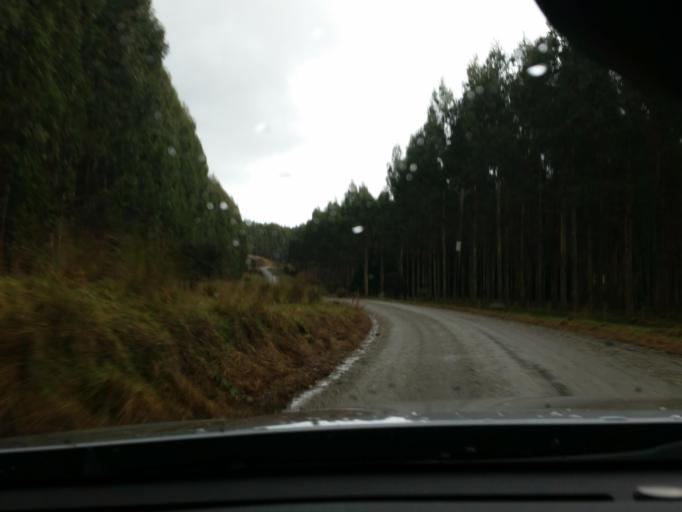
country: NZ
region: Southland
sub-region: Gore District
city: Gore
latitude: -46.5086
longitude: 168.9316
